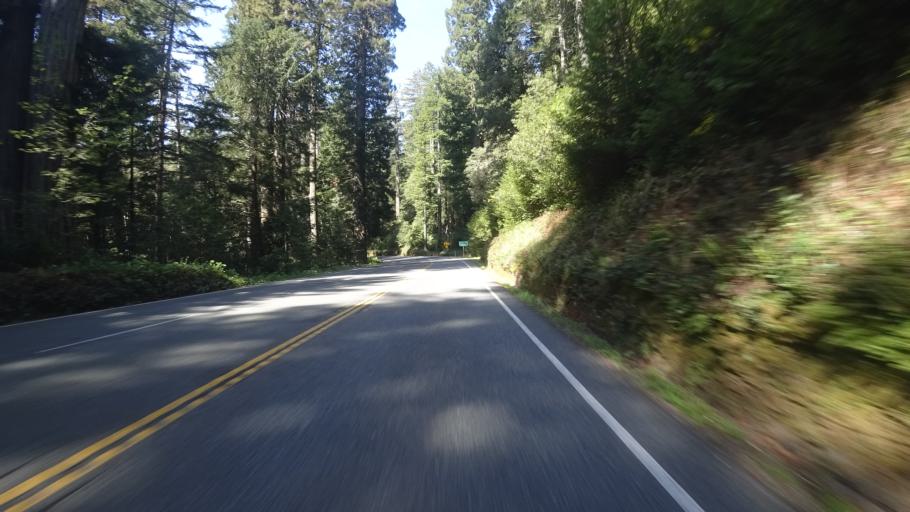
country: US
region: California
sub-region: Del Norte County
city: Bertsch-Oceanview
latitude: 41.6837
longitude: -124.1110
